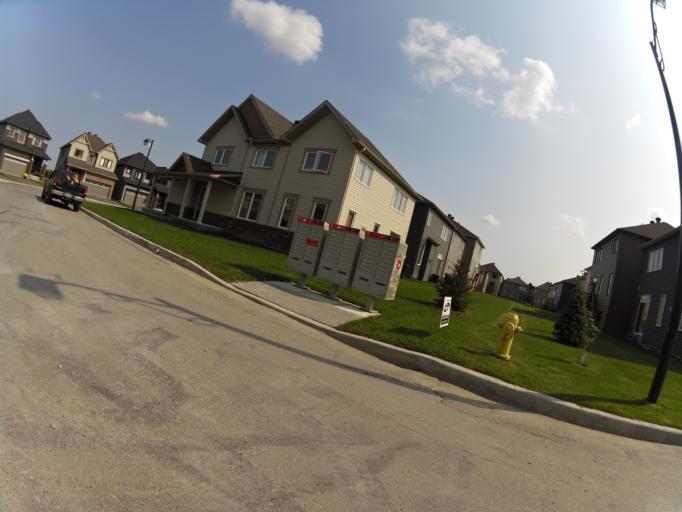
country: CA
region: Ontario
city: Bells Corners
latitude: 45.3064
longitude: -75.9388
